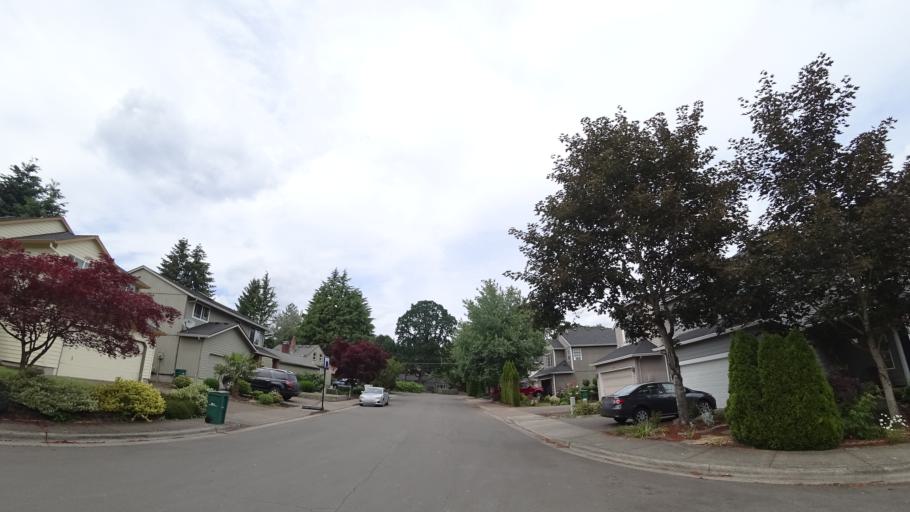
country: US
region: Oregon
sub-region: Washington County
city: Metzger
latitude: 45.4520
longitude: -122.7636
